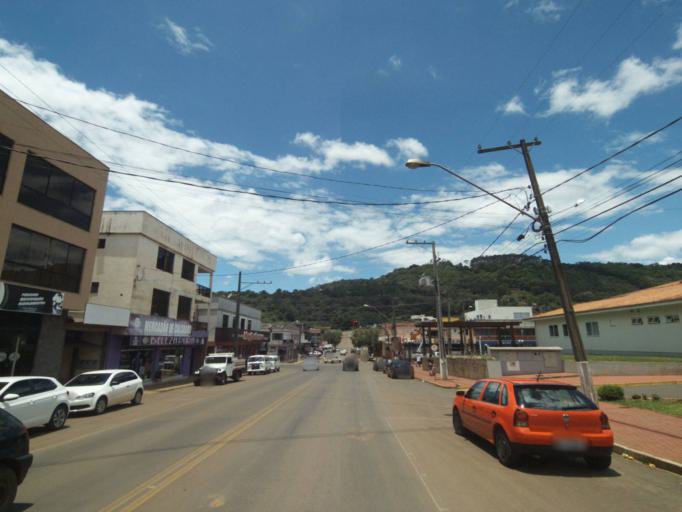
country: BR
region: Parana
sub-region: Pinhao
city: Pinhao
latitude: -26.1569
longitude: -51.5555
